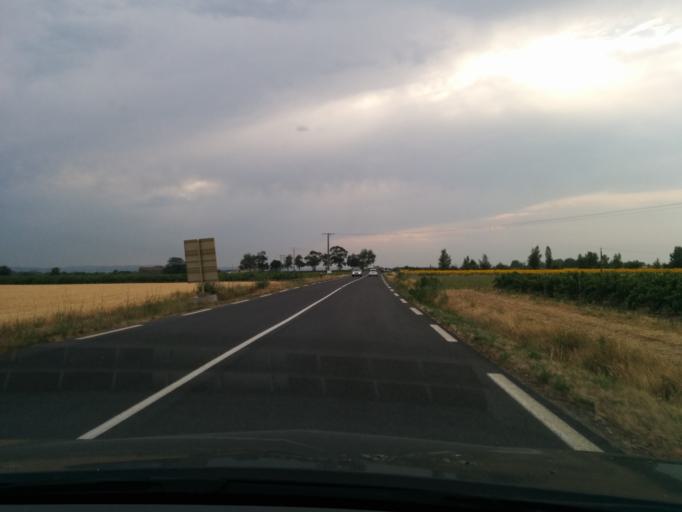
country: FR
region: Languedoc-Roussillon
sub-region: Departement de l'Aude
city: Alzonne
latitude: 43.2551
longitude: 2.1637
